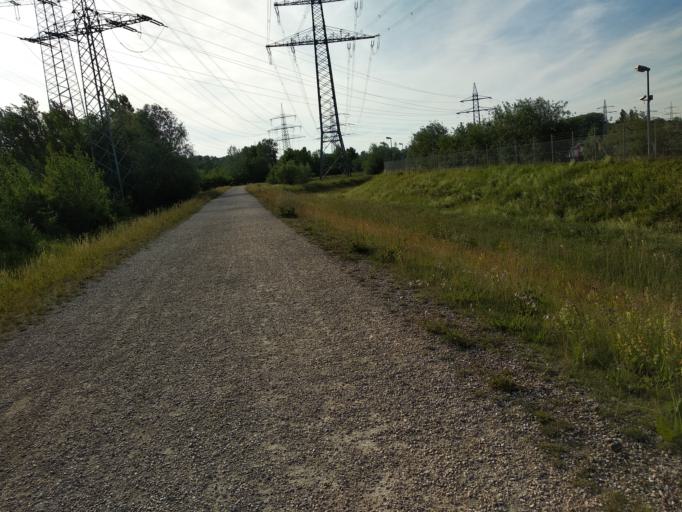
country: DE
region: Bavaria
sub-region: Swabia
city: Vohringen
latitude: 48.2696
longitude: 10.0704
